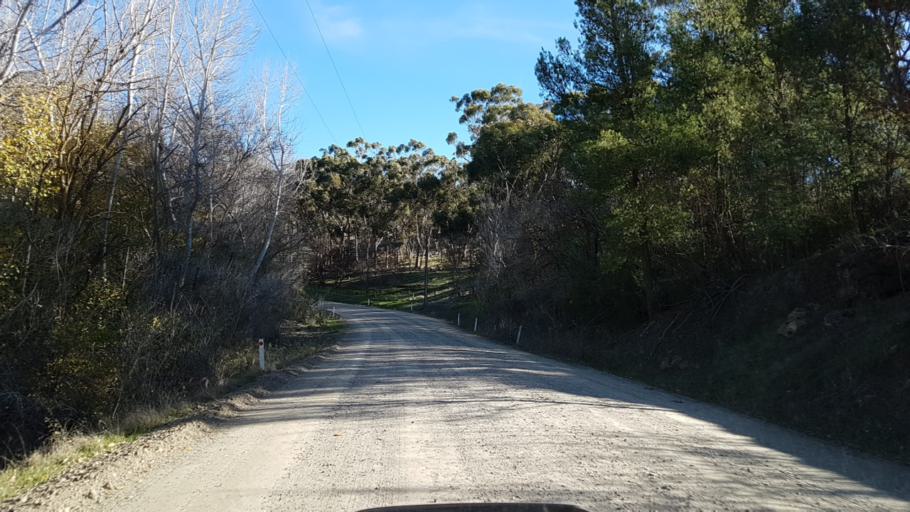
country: AU
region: South Australia
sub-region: Northern Areas
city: Jamestown
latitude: -33.2781
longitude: 138.5682
